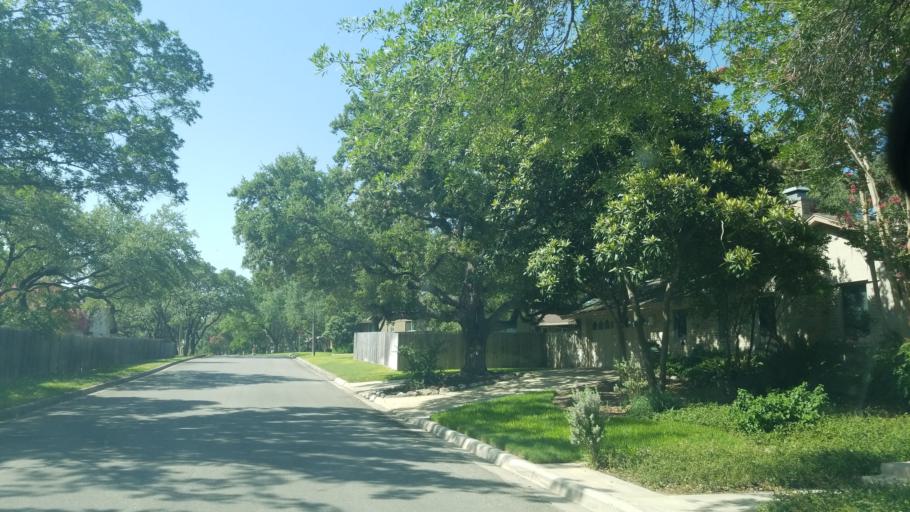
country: US
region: Texas
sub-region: Bexar County
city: Hollywood Park
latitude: 29.6046
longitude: -98.4845
